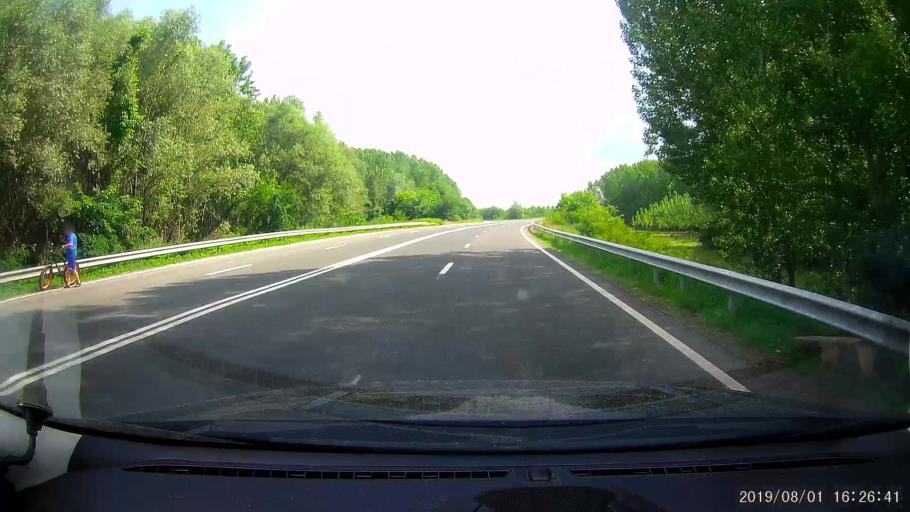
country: RO
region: Calarasi
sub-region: Municipiul Calarasi
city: Calarasi
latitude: 44.1750
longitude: 27.3203
